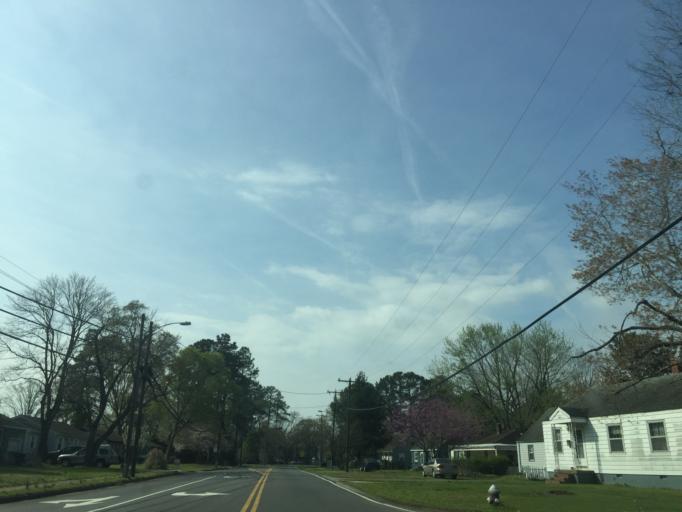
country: US
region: Virginia
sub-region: City of Newport News
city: Newport News
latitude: 37.0739
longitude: -76.4576
